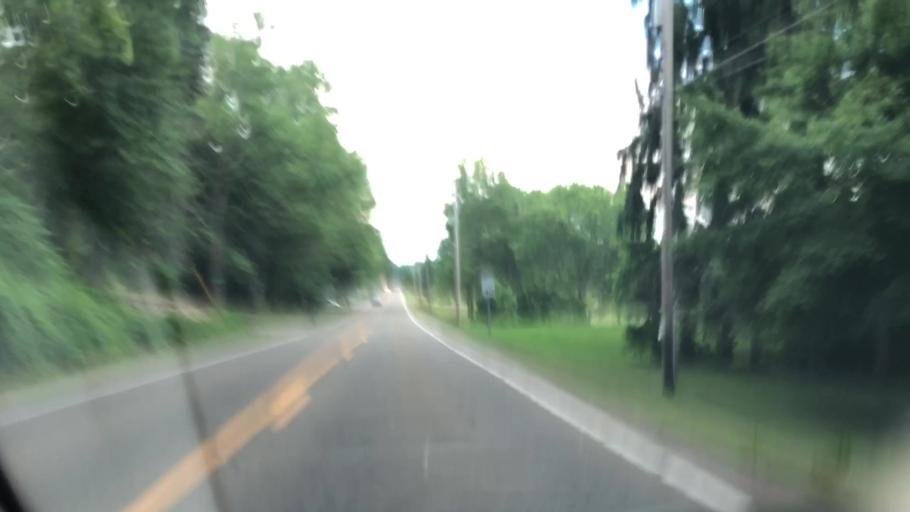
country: US
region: Ohio
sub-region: Summit County
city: Portage Lakes
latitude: 41.0031
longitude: -81.5626
